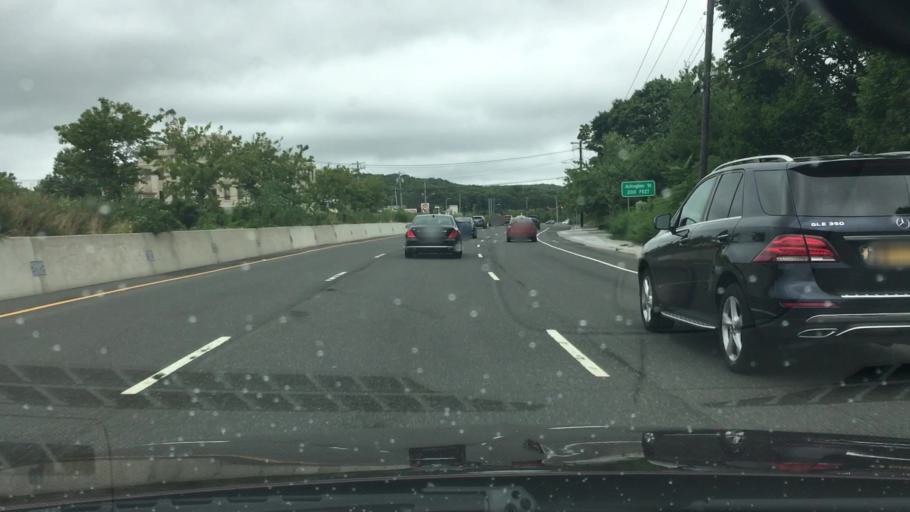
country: US
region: New York
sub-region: Suffolk County
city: Melville
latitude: 40.7910
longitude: -73.4153
